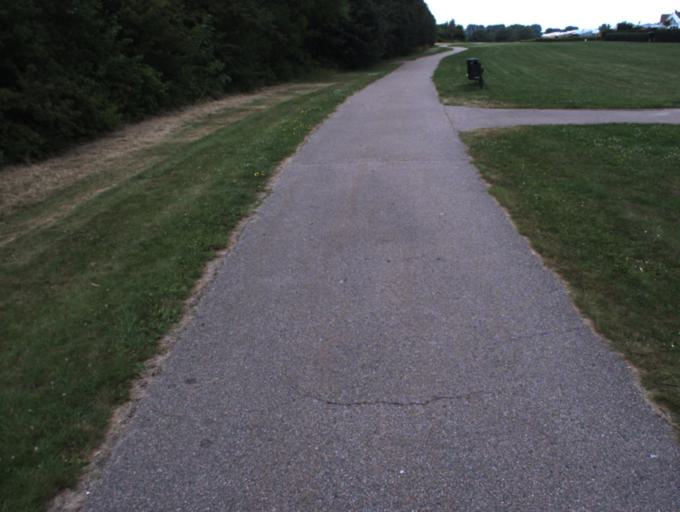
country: SE
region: Skane
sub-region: Helsingborg
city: Rydeback
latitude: 55.9601
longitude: 12.7595
